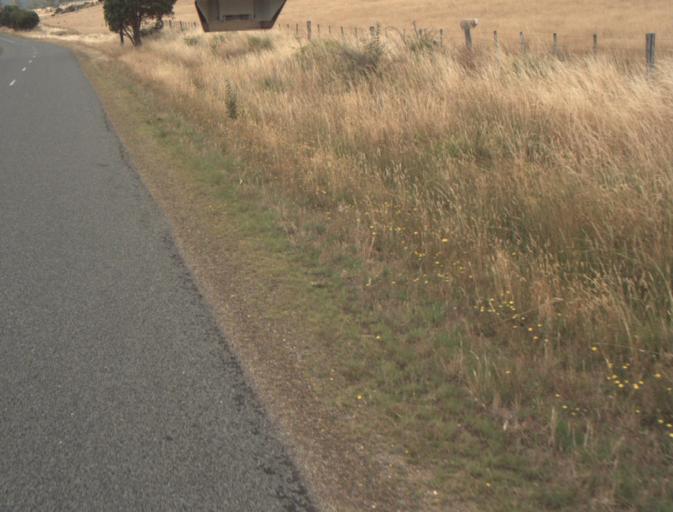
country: AU
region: Tasmania
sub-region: Northern Midlands
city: Evandale
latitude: -41.4977
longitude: 147.4537
